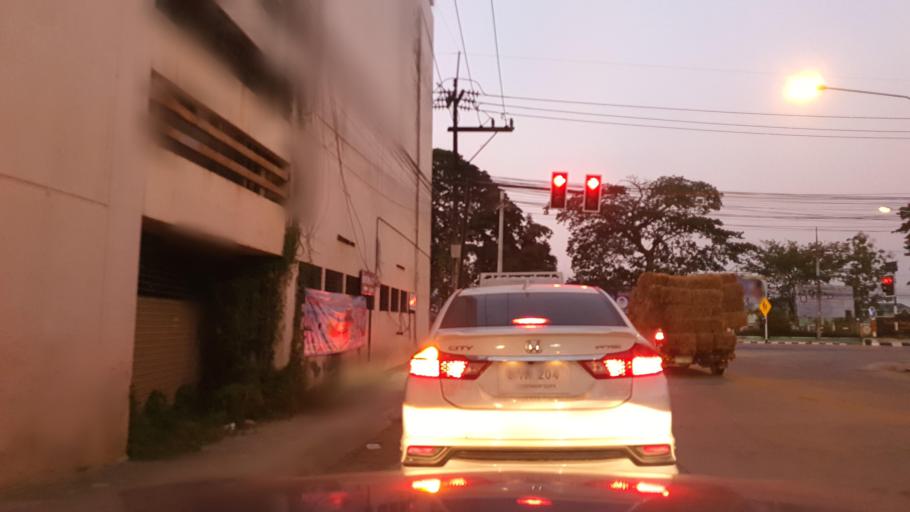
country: TH
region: Phayao
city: Dok Kham Tai
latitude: 19.1626
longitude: 99.9923
